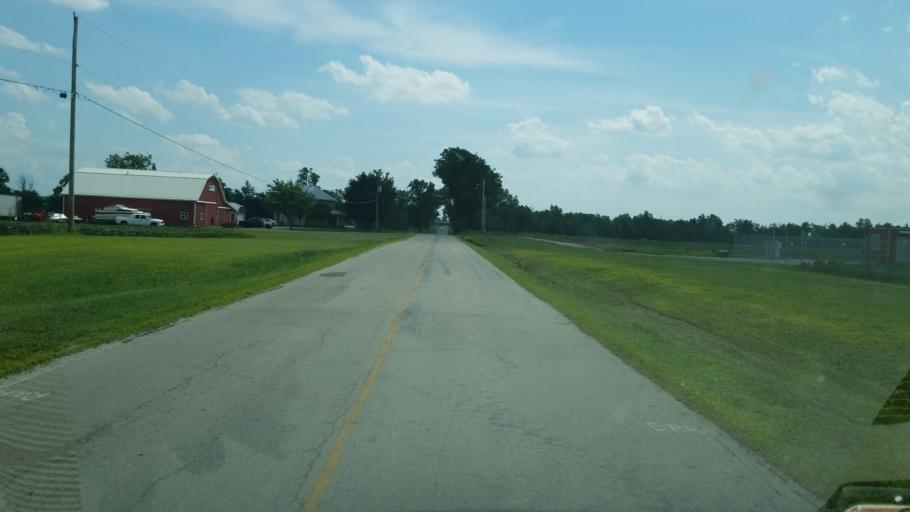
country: US
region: Ohio
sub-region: Hardin County
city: Forest
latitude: 40.8249
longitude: -83.4774
